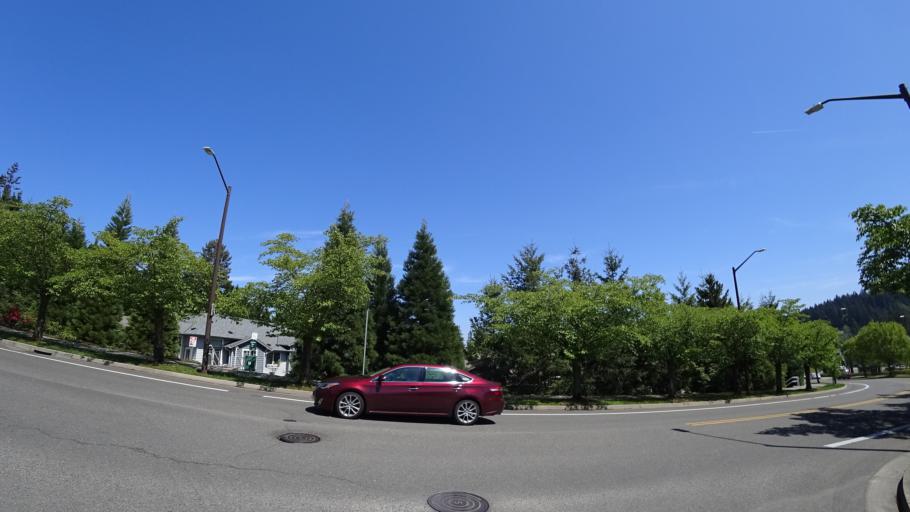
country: US
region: Oregon
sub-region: Washington County
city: King City
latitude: 45.4322
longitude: -122.8317
